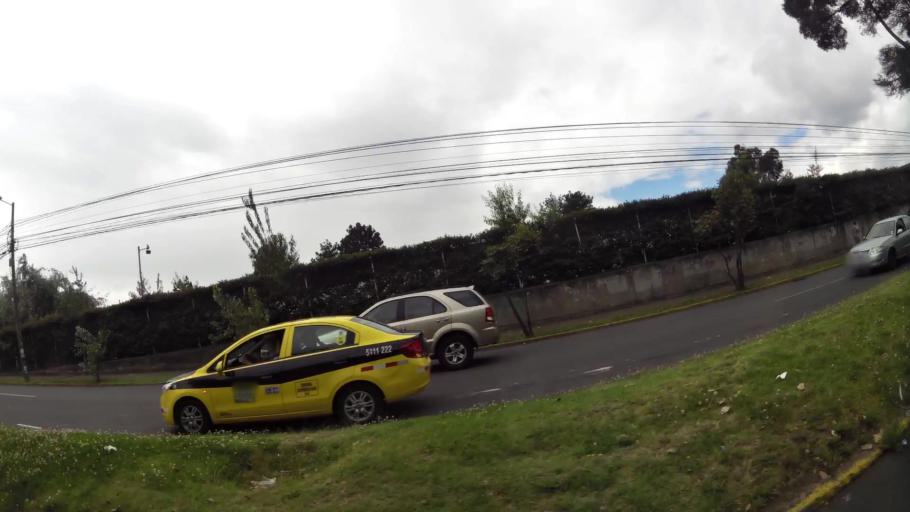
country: EC
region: Pichincha
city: Quito
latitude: -0.1606
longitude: -78.4900
